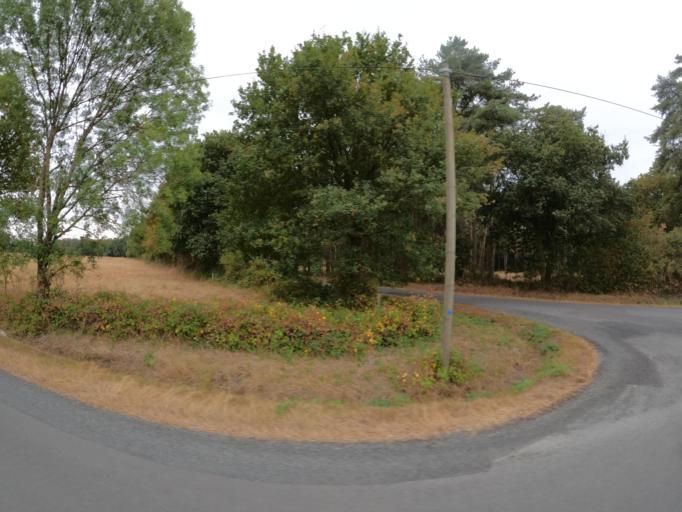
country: FR
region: Pays de la Loire
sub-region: Departement de la Vendee
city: La Boissiere-de-Montaigu
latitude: 46.9764
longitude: -1.1929
